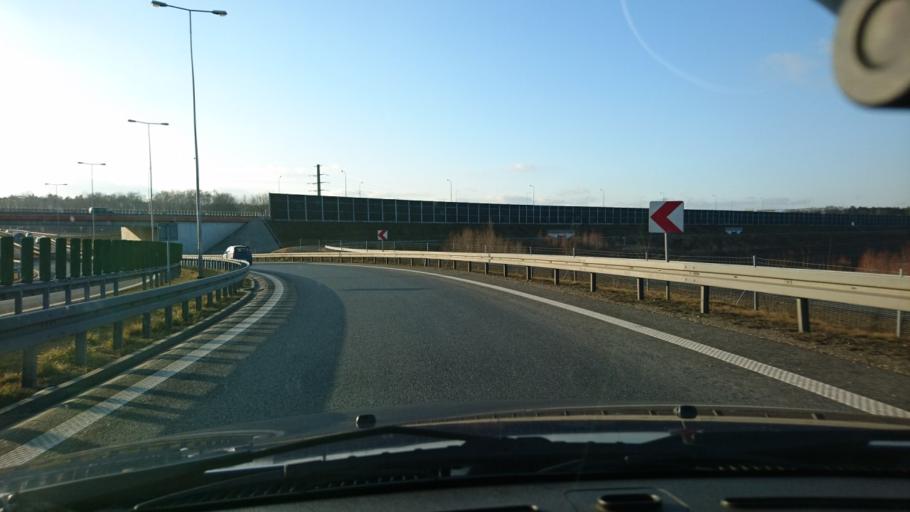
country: PL
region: Silesian Voivodeship
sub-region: Gliwice
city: Gliwice
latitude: 50.3113
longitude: 18.7282
